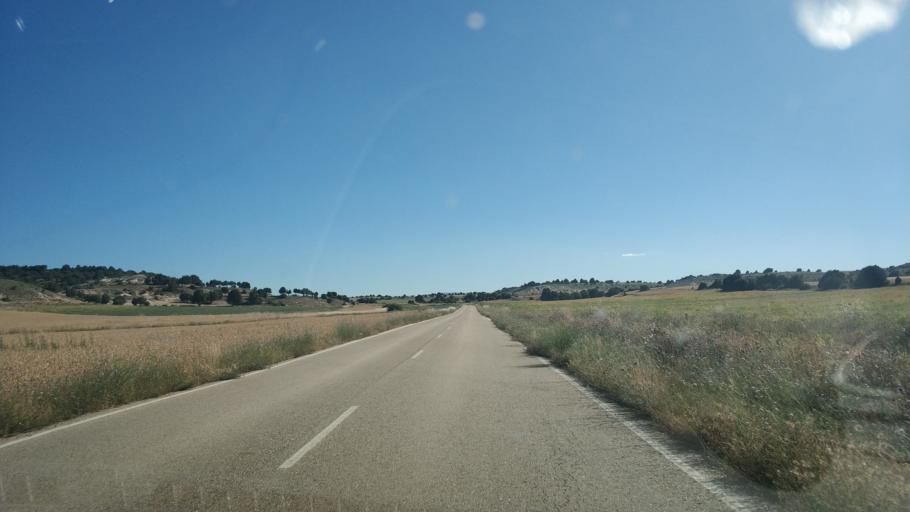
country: ES
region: Castille and Leon
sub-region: Provincia de Soria
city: San Esteban de Gormaz
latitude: 41.4830
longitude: -3.2120
